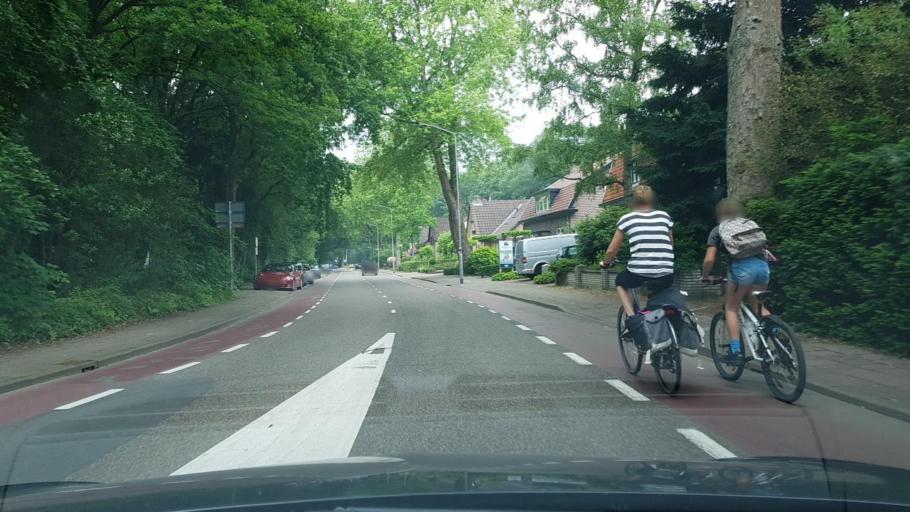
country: NL
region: Gelderland
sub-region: Gemeente Ermelo
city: Ermelo
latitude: 52.3035
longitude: 5.6201
